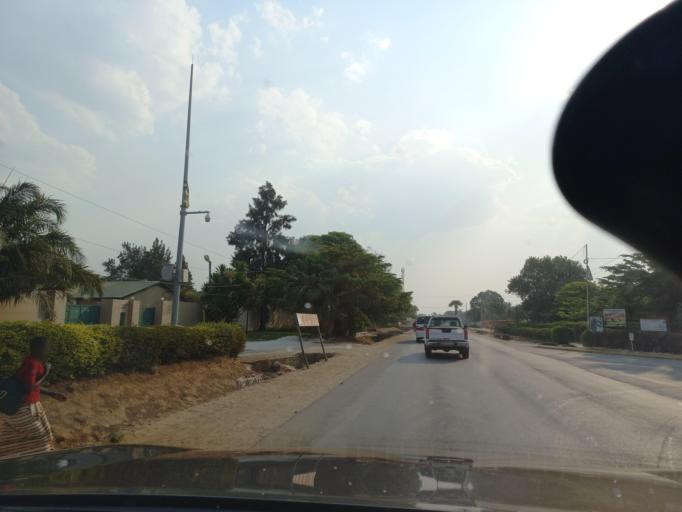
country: ZM
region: Lusaka
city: Lusaka
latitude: -15.4599
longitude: 28.2533
